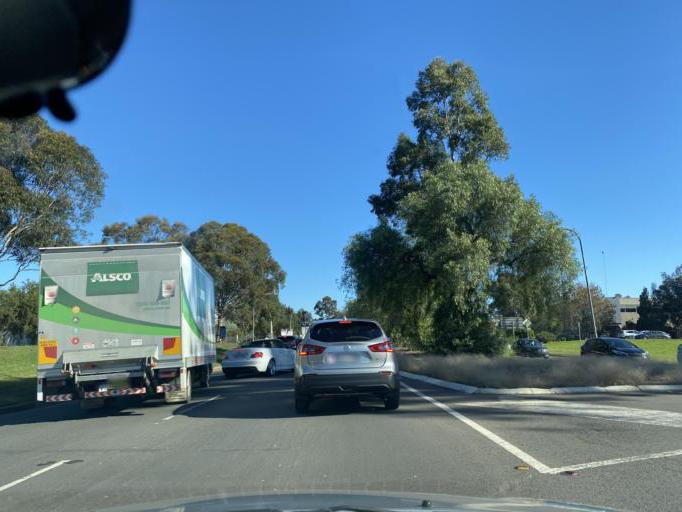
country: AU
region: New South Wales
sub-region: Campbelltown Municipality
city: Ingleburn
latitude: -33.9893
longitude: 150.8595
